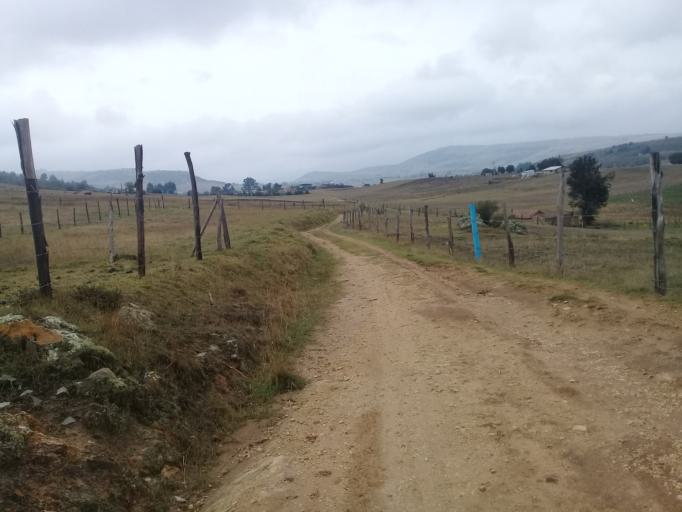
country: CO
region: Boyaca
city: Siachoque
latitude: 5.5644
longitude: -73.2755
